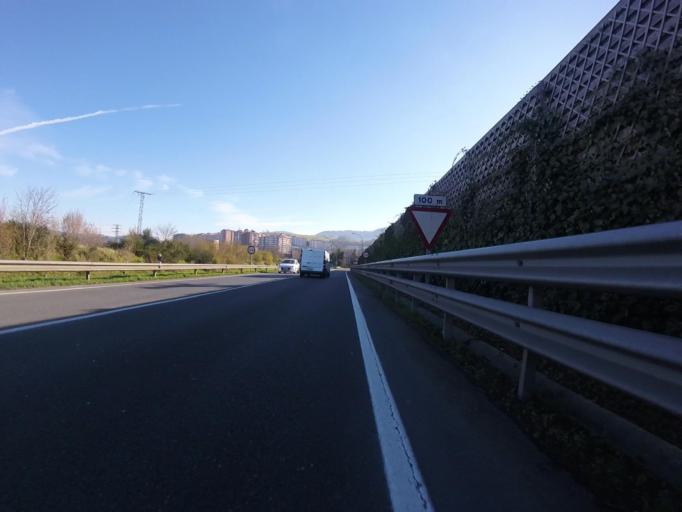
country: ES
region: Basque Country
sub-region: Provincia de Guipuzcoa
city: Irun
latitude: 43.3414
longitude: -1.7823
